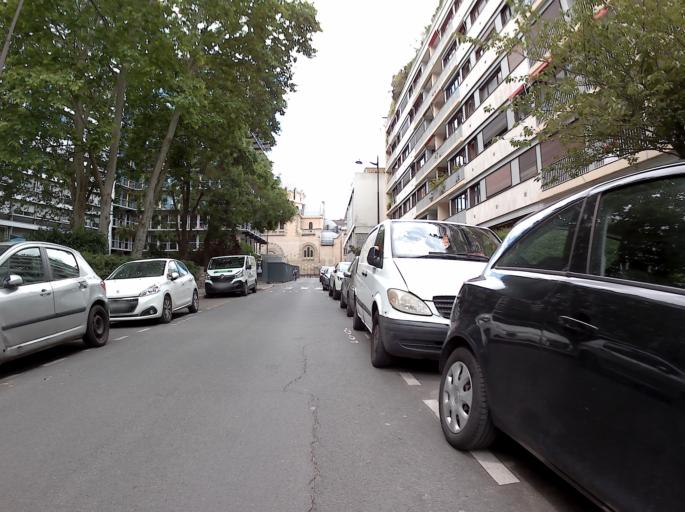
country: FR
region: Ile-de-France
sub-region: Departement du Val-de-Marne
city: Gentilly
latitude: 48.8317
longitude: 2.3366
